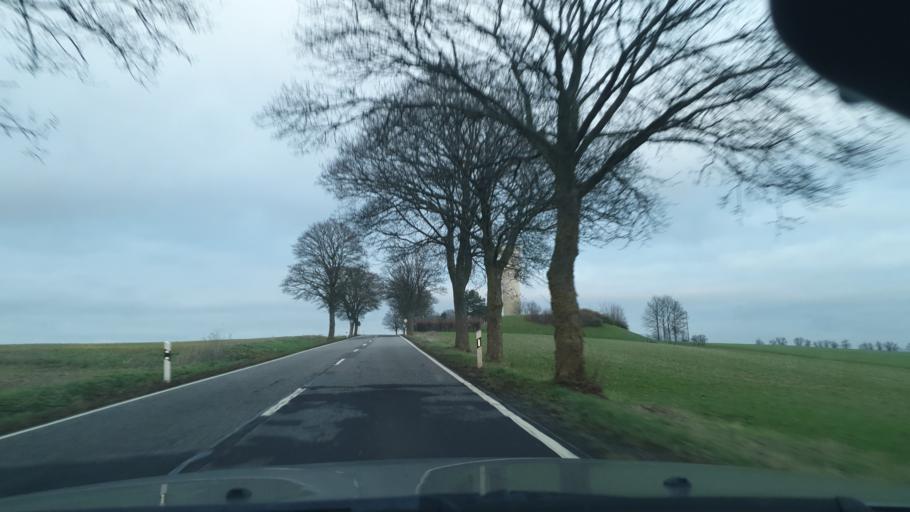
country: DE
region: Rheinland-Pfalz
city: Kashofen
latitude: 49.3196
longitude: 7.4073
